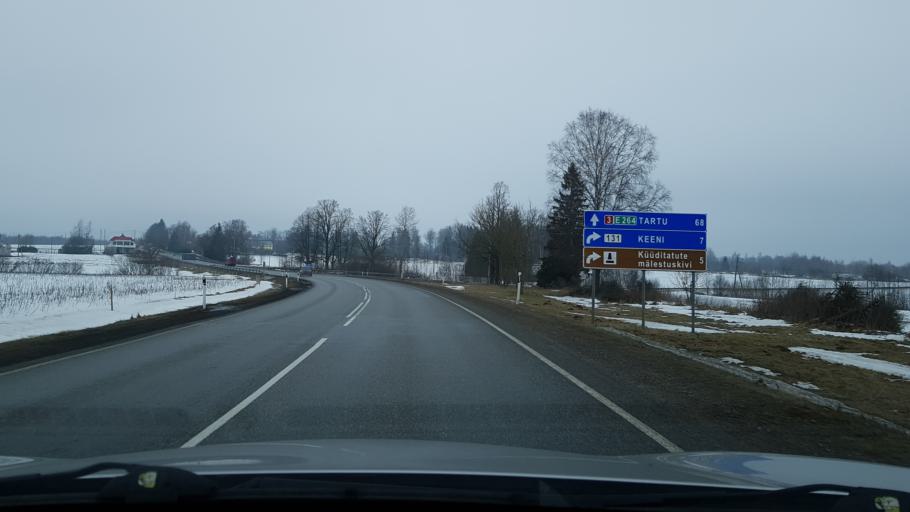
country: EE
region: Valgamaa
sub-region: Valga linn
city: Valga
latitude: 57.9198
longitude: 26.1823
